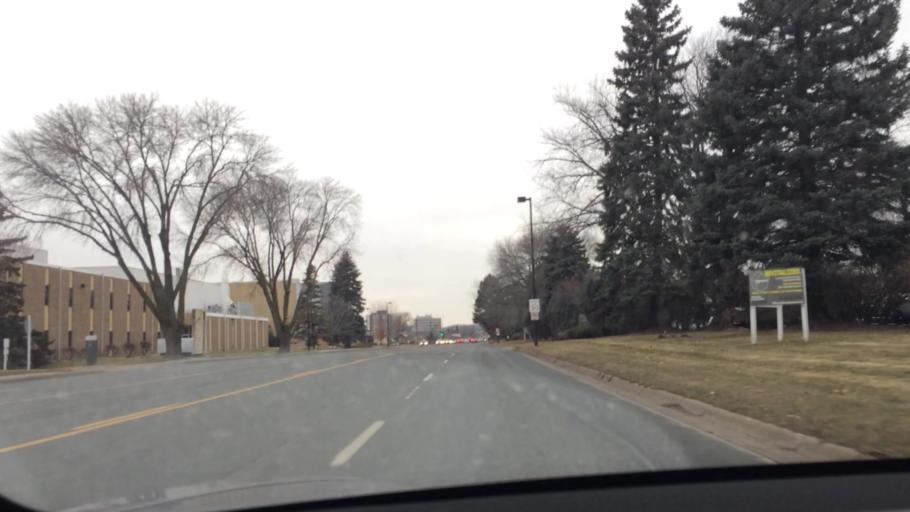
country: US
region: Minnesota
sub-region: Hennepin County
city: Edina
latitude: 44.8633
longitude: -93.3410
